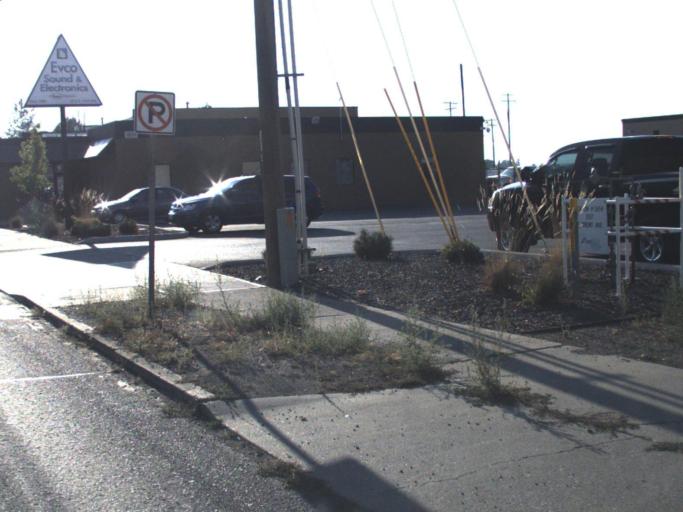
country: US
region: Washington
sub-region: Spokane County
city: Spokane
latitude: 47.6694
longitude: -117.3576
